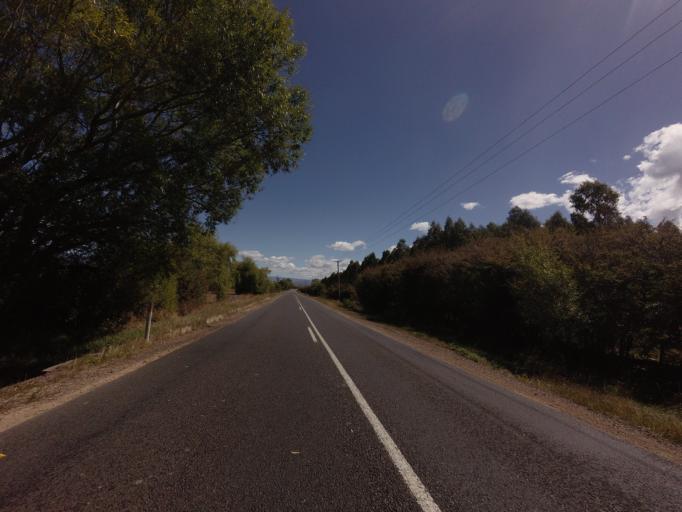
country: AU
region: Tasmania
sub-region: Break O'Day
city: St Helens
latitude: -41.5782
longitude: 148.1428
